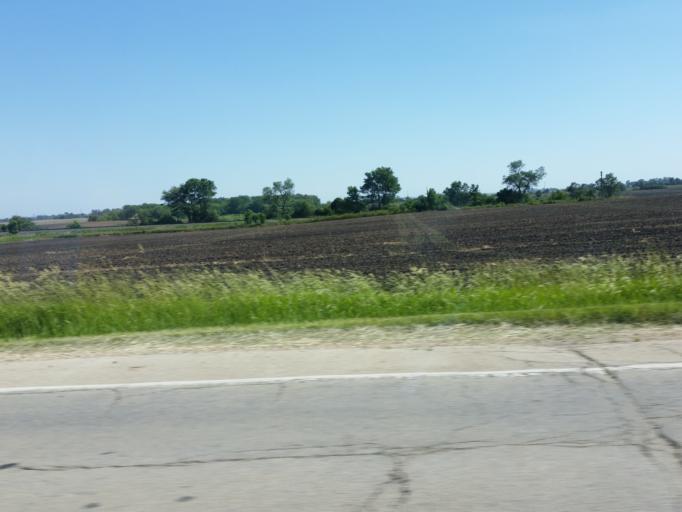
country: US
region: Illinois
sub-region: Ogle County
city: Davis Junction
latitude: 42.1003
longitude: -89.0654
